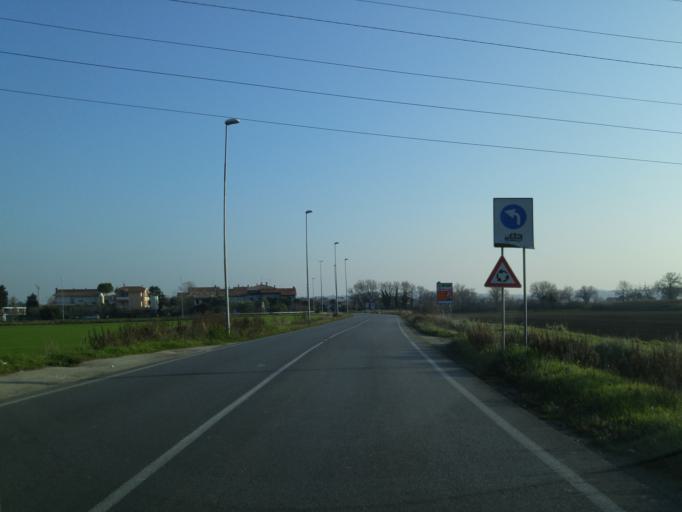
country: IT
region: The Marches
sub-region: Provincia di Pesaro e Urbino
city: Rosciano
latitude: 43.8059
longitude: 12.9857
